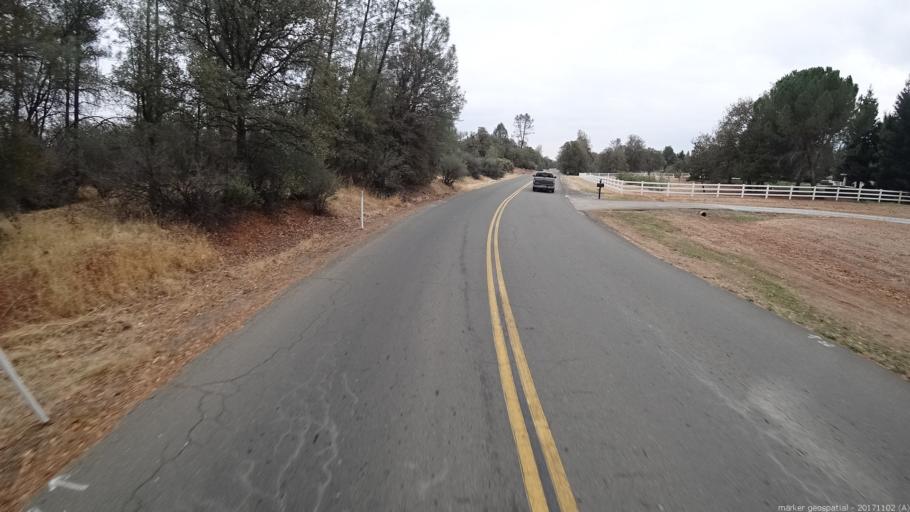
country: US
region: California
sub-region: Shasta County
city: Shasta Lake
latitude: 40.6582
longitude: -122.3198
